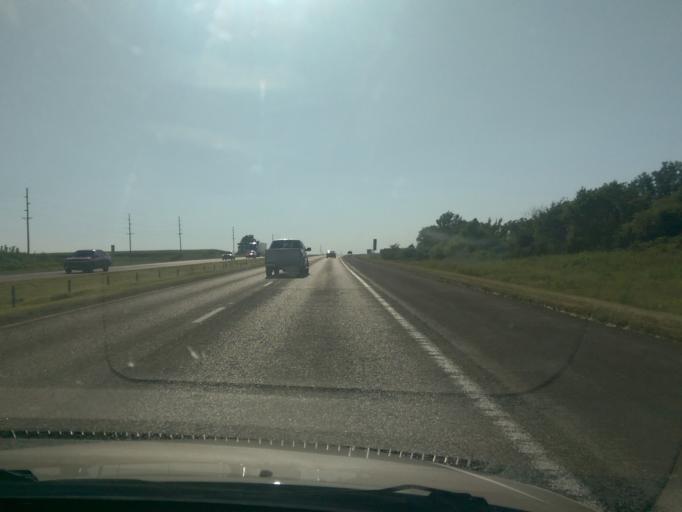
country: US
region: Missouri
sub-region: Lafayette County
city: Higginsville
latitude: 38.9929
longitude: -93.7040
